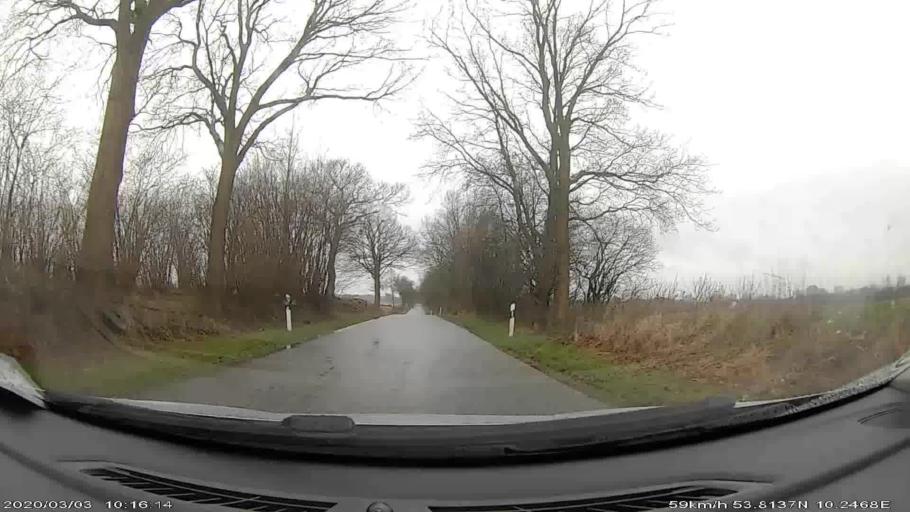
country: DE
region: Schleswig-Holstein
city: Sulfeld
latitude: 53.8094
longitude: 10.2443
